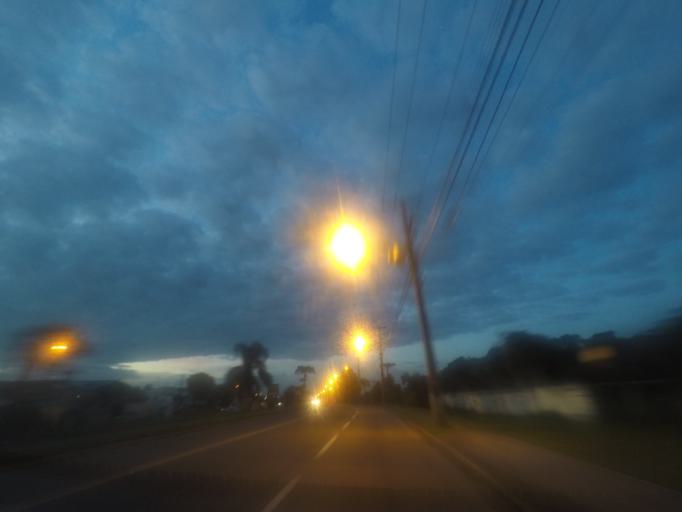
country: BR
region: Parana
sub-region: Pinhais
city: Pinhais
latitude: -25.3979
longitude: -49.1891
